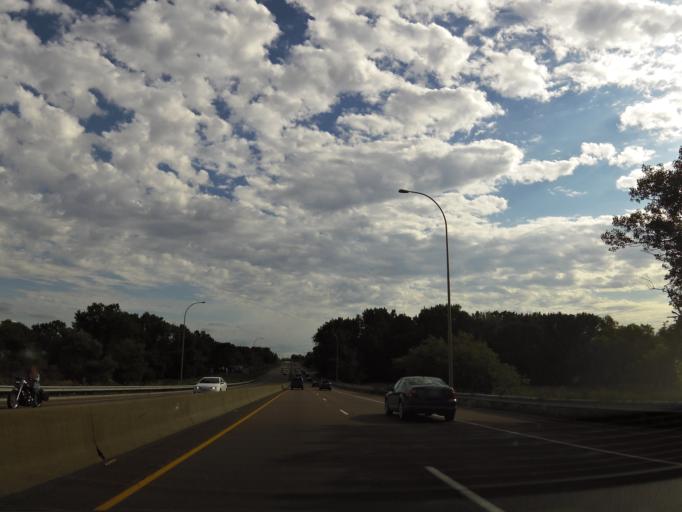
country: US
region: Minnesota
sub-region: Hennepin County
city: Minnetonka Mills
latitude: 44.9631
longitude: -93.4007
